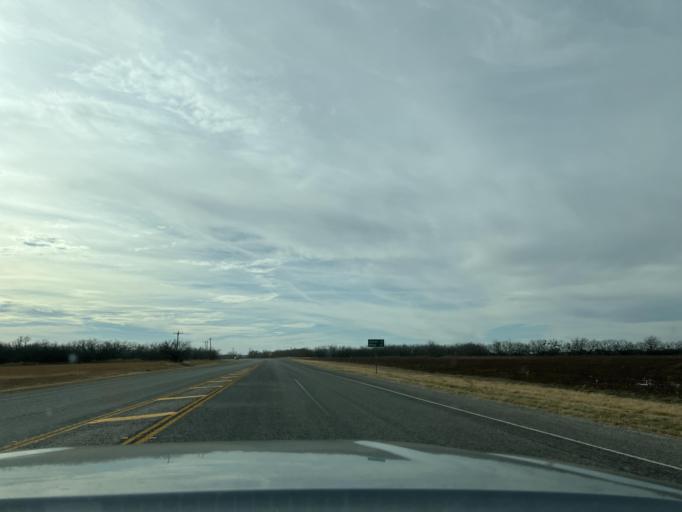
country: US
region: Texas
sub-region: Jones County
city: Stamford
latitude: 32.7660
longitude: -99.5930
